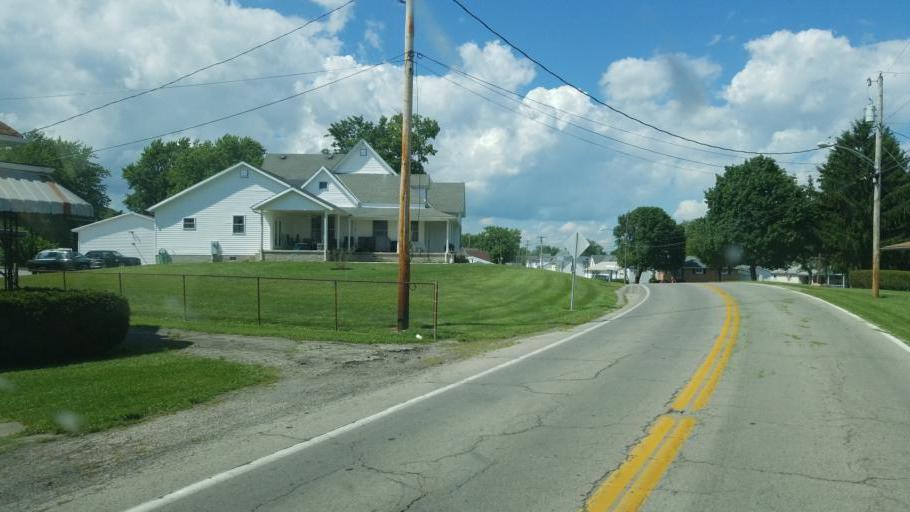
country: US
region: Ohio
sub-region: Highland County
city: Greenfield
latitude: 39.3430
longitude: -83.3905
